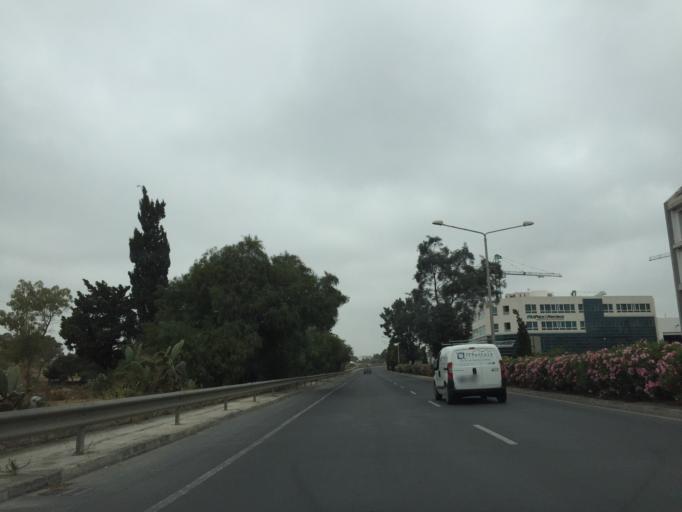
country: MT
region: Birkirkara
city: Birkirkara
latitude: 35.8893
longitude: 14.4613
